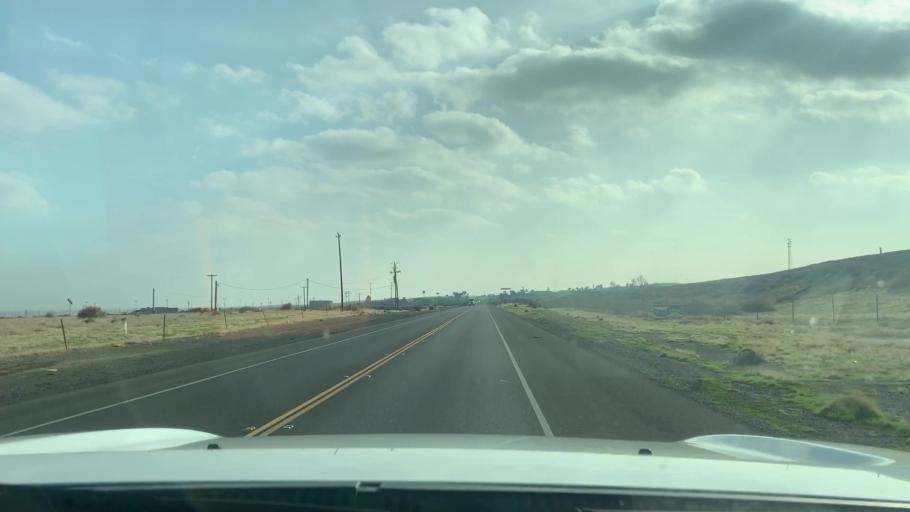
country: US
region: California
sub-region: Kings County
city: Kettleman City
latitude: 35.9980
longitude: -119.9595
